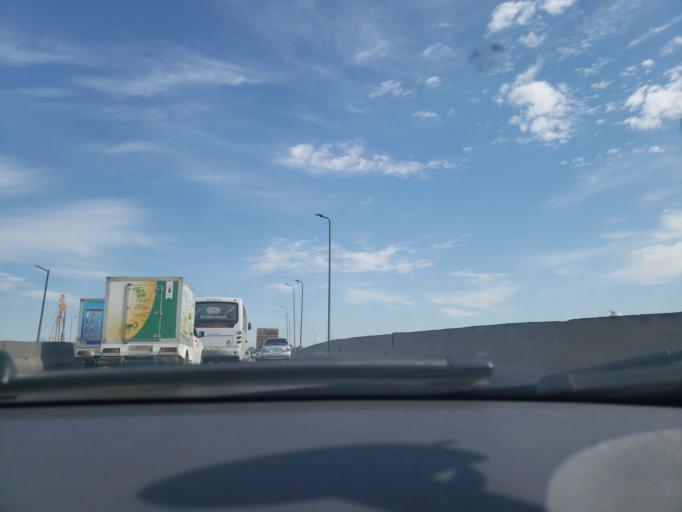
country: EG
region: Muhafazat al Qalyubiyah
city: Al Khankah
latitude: 30.1491
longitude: 31.4307
